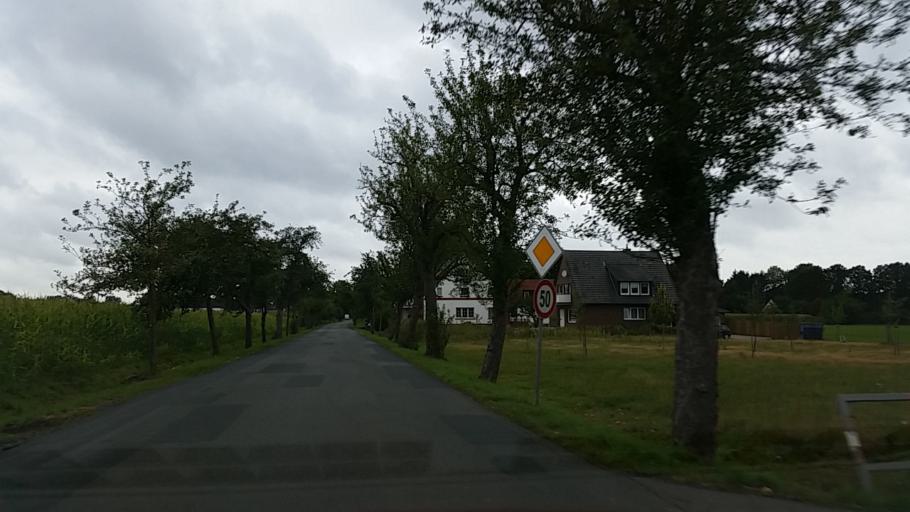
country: DE
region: North Rhine-Westphalia
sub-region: Regierungsbezirk Munster
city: Lotte
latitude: 52.2917
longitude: 7.9367
